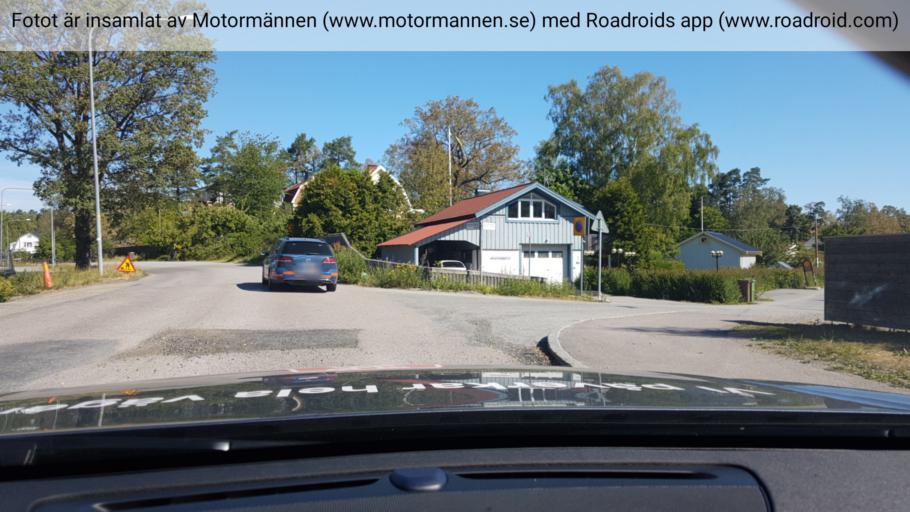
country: SE
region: Stockholm
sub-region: Huddinge Kommun
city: Huddinge
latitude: 59.2335
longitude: 17.9974
